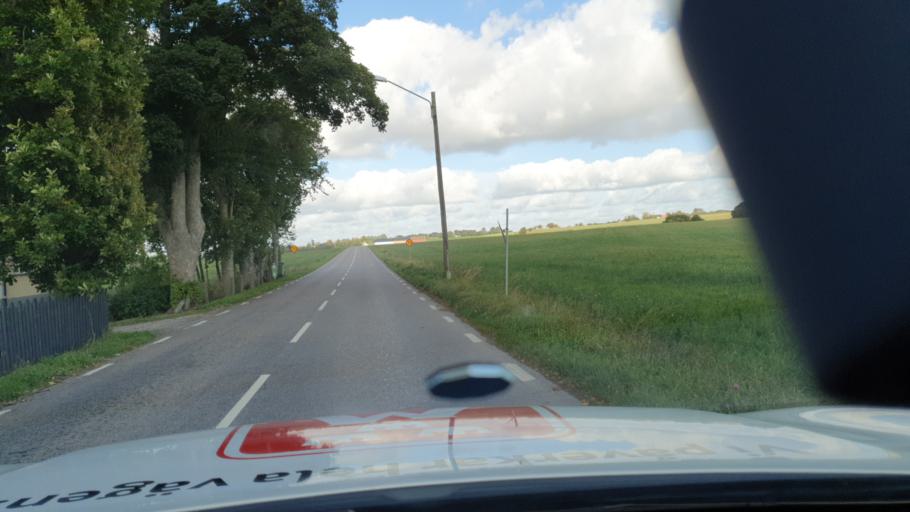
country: SE
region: Skane
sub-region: Ystads Kommun
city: Kopingebro
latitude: 55.4844
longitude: 13.9502
